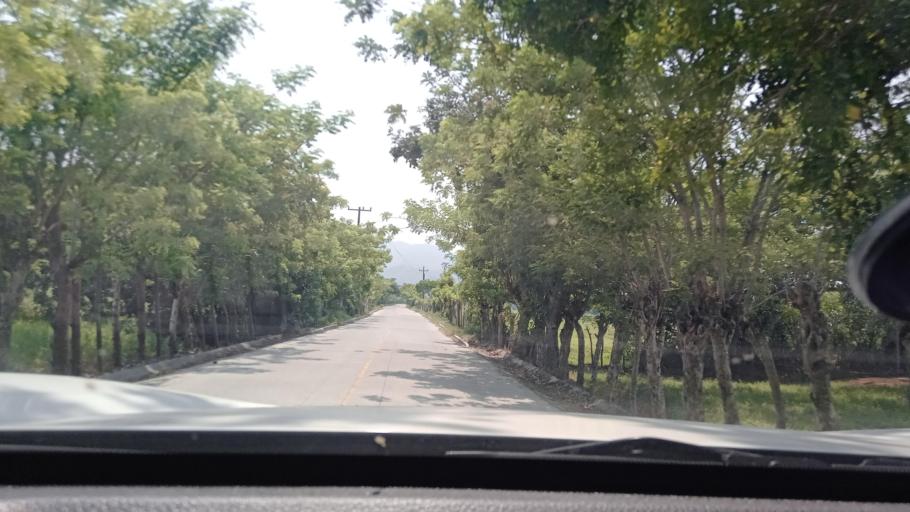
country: MX
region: Veracruz
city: Catemaco
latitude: 18.5621
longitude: -95.0416
